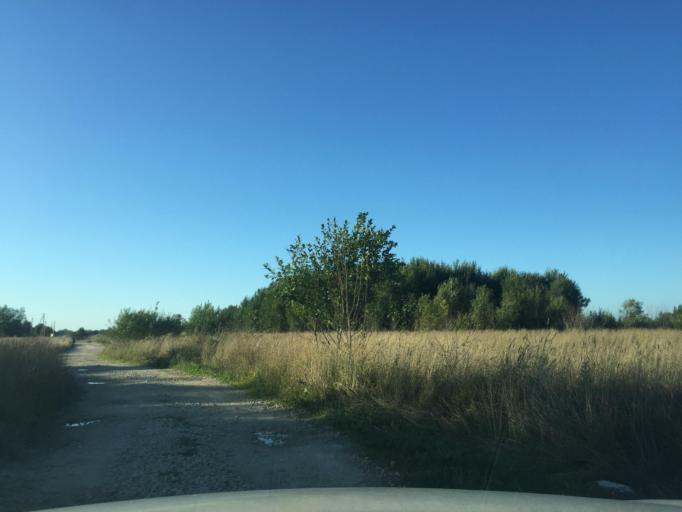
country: RU
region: Leningrad
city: Rozhdestveno
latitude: 59.3297
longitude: 29.9982
